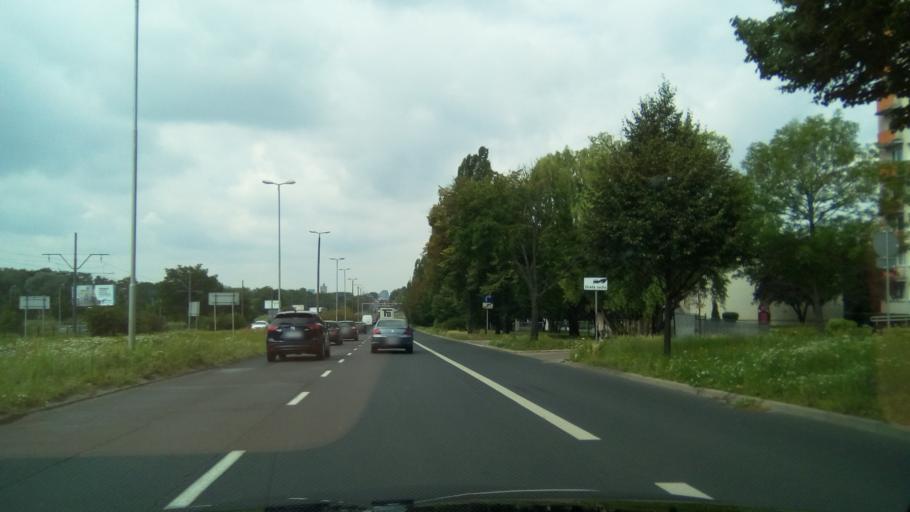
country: PL
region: Greater Poland Voivodeship
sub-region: Poznan
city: Poznan
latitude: 52.4096
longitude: 16.9784
